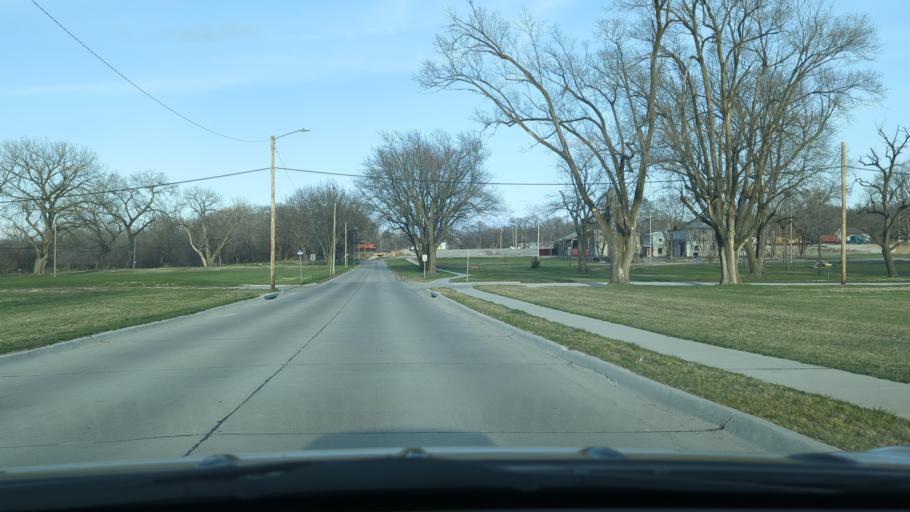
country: US
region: Nebraska
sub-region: Saunders County
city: Ashland
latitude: 41.0391
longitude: -96.3629
